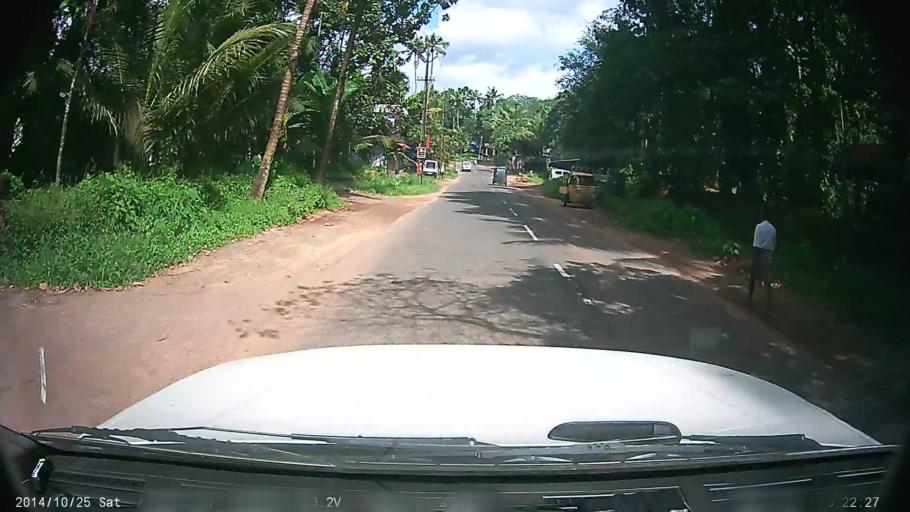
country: IN
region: Kerala
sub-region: Ernakulam
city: Muvattupuzha
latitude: 9.9018
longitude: 76.5871
